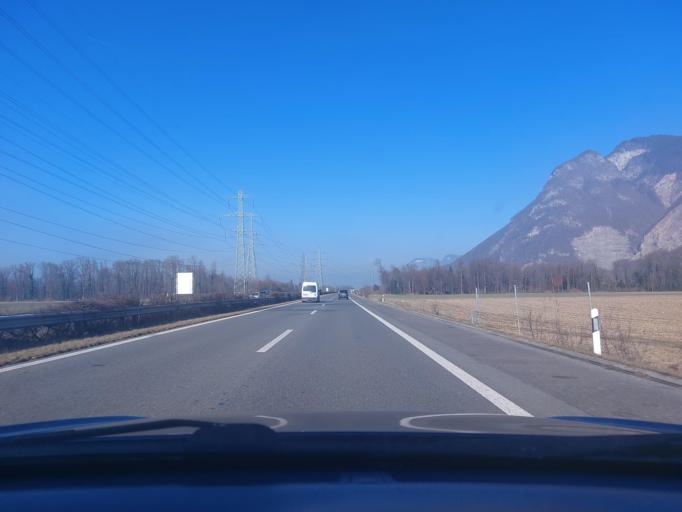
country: CH
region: Valais
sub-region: Monthey District
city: Vouvry
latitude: 46.3450
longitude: 6.9286
